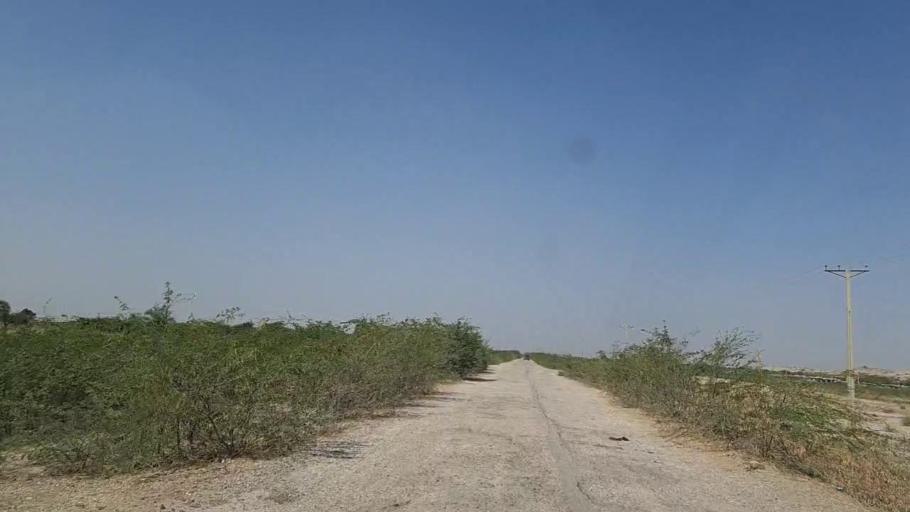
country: PK
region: Sindh
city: Naukot
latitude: 24.6321
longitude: 69.2883
